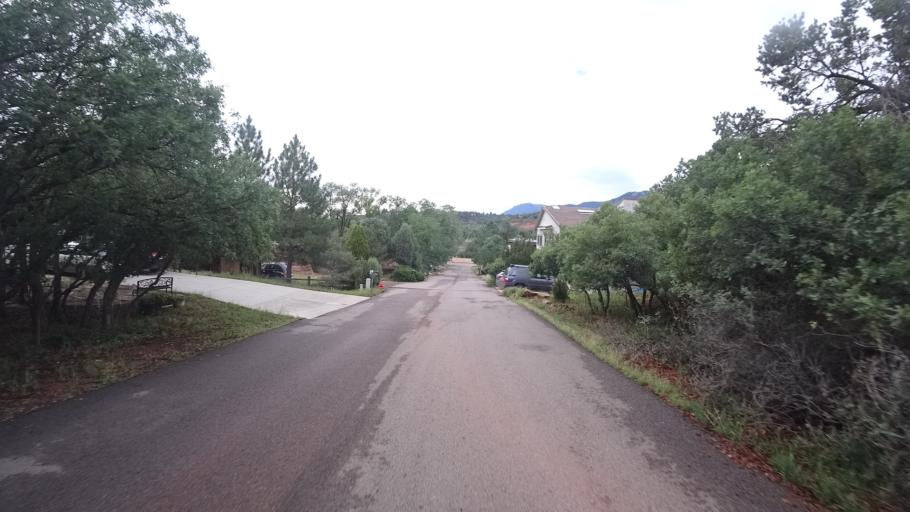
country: US
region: Colorado
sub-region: El Paso County
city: Manitou Springs
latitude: 38.8620
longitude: -104.8946
